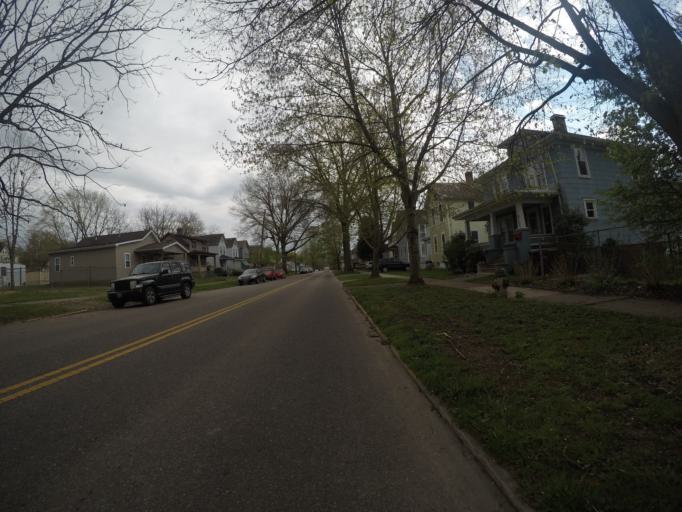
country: US
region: Ohio
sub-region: Washington County
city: Marietta
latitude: 39.4254
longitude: -81.4672
